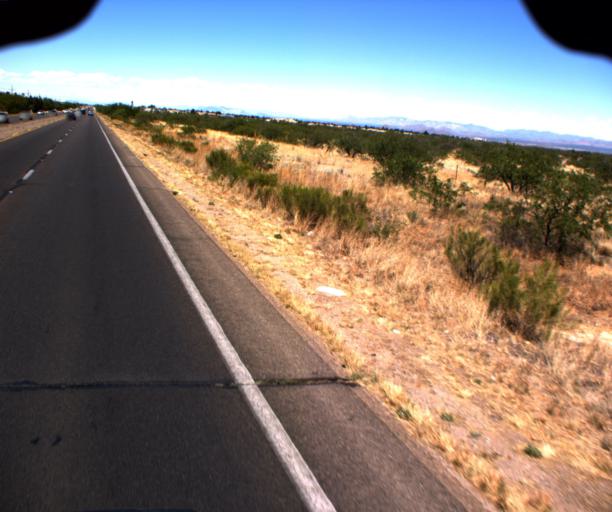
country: US
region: Arizona
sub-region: Cochise County
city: Sierra Vista
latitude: 31.5191
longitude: -110.2573
